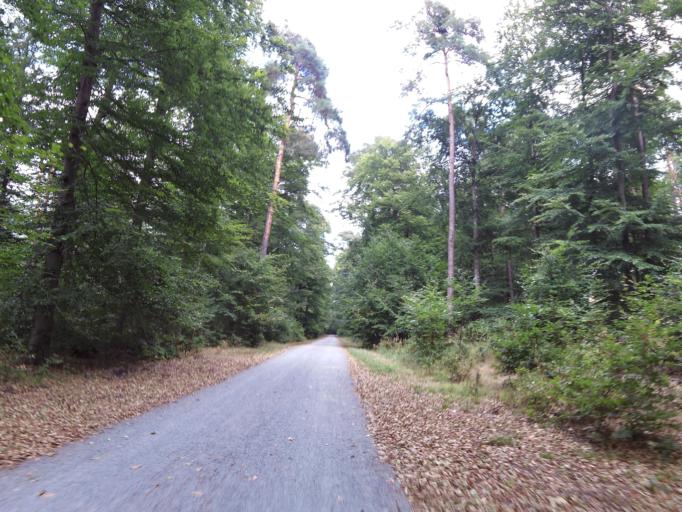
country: DE
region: Hesse
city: Morfelden-Walldorf
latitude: 49.9993
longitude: 8.5566
